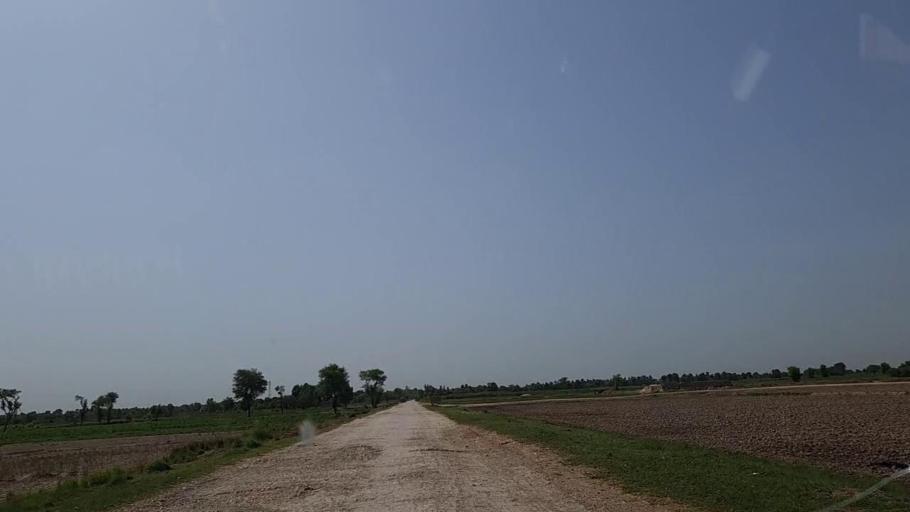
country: PK
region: Sindh
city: Naushahro Firoz
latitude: 26.8379
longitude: 68.0169
